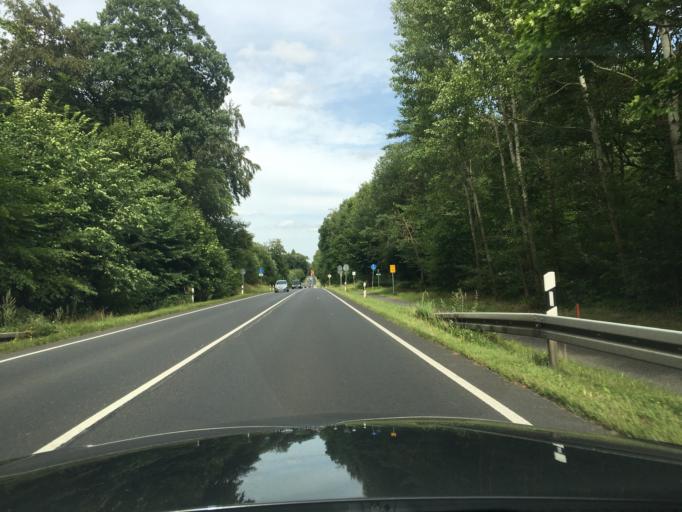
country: DE
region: Mecklenburg-Vorpommern
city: Neustrelitz
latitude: 53.3871
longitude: 13.0914
